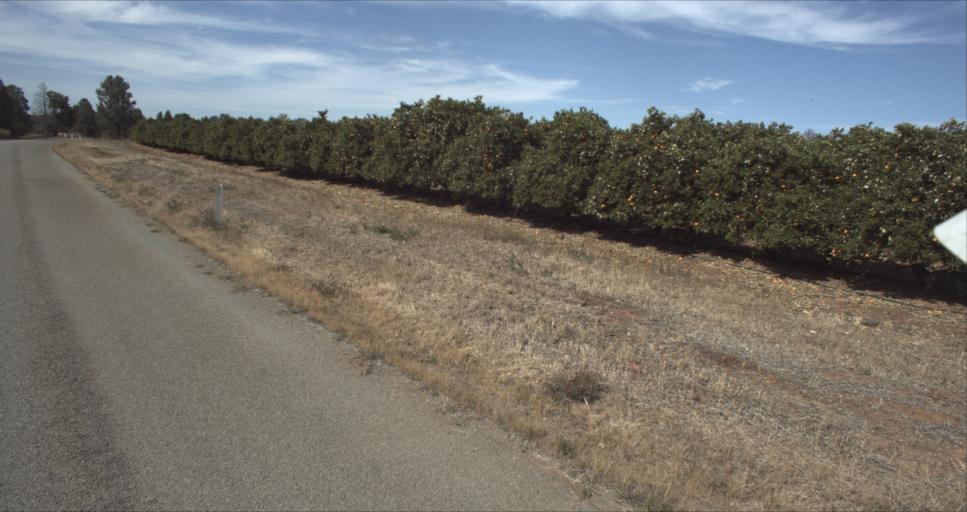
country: AU
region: New South Wales
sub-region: Leeton
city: Leeton
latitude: -34.5838
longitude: 146.4609
